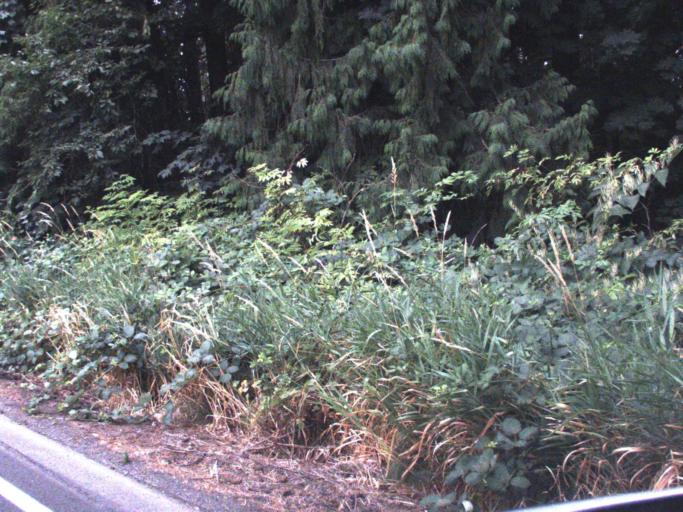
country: US
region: Washington
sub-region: King County
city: Carnation
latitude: 47.6253
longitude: -121.9097
